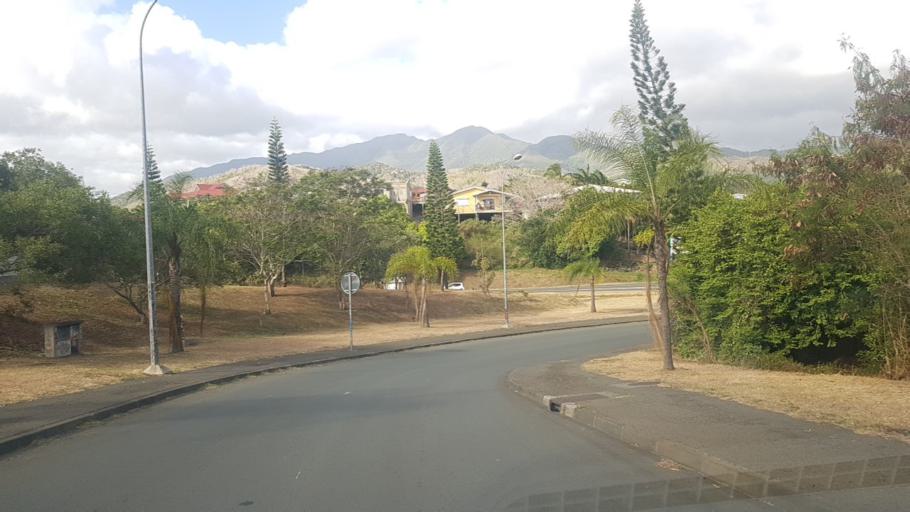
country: NC
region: South Province
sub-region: Noumea
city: Noumea
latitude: -22.2153
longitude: 166.4789
